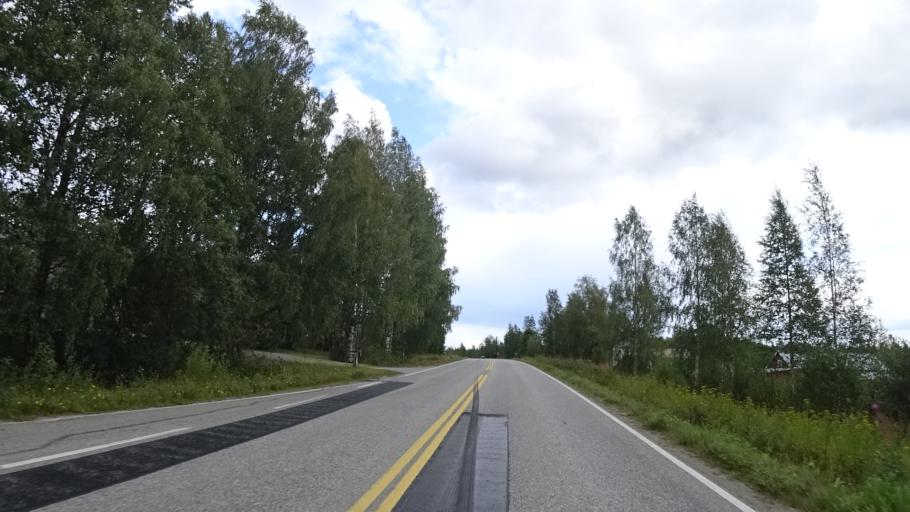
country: FI
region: North Karelia
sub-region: Joensuu
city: Ilomantsi
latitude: 62.6488
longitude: 30.9923
